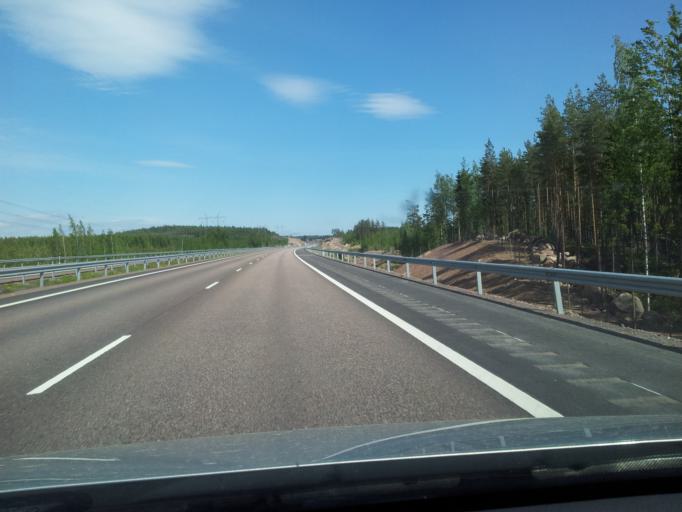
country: FI
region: Uusimaa
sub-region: Loviisa
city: Lovisa
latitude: 60.4899
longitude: 26.3354
